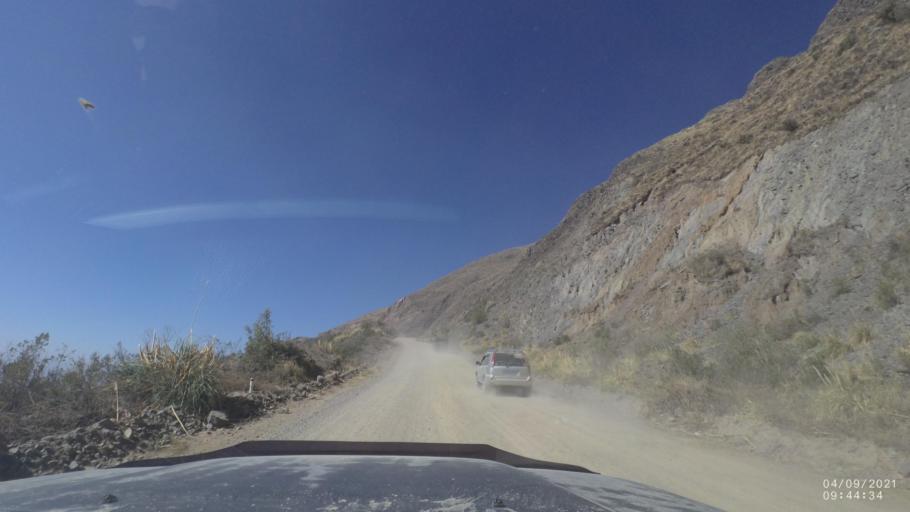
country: BO
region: Cochabamba
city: Sipe Sipe
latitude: -17.3426
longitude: -66.3904
